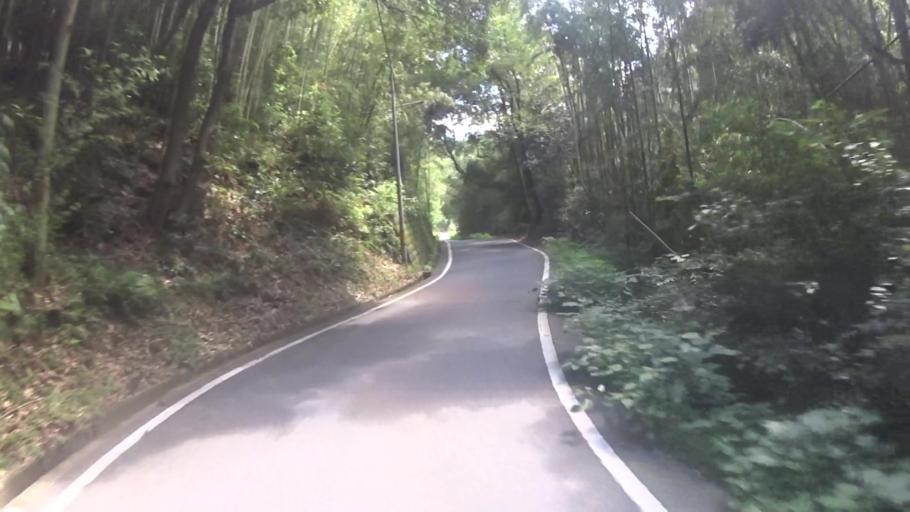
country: JP
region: Nara
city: Nara-shi
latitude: 34.7264
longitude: 135.8871
